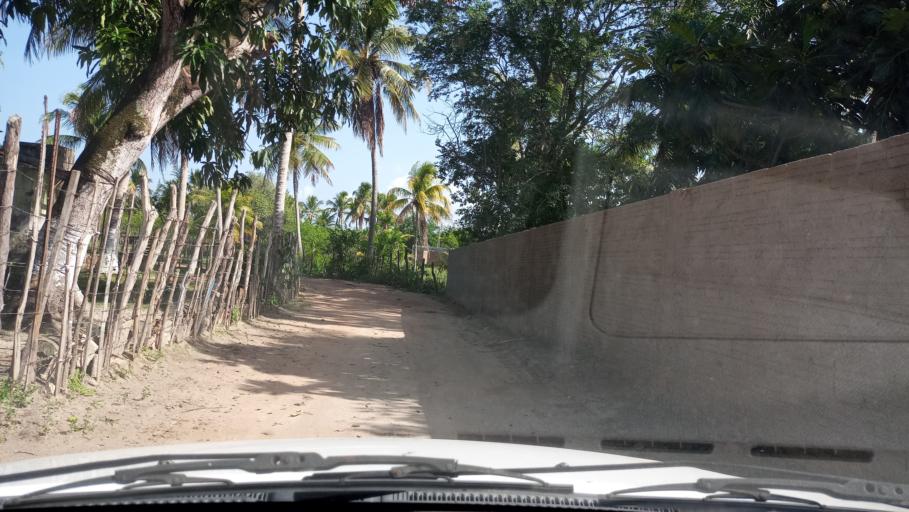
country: BR
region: Rio Grande do Norte
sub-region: Ares
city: Ares
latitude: -6.2229
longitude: -35.1508
